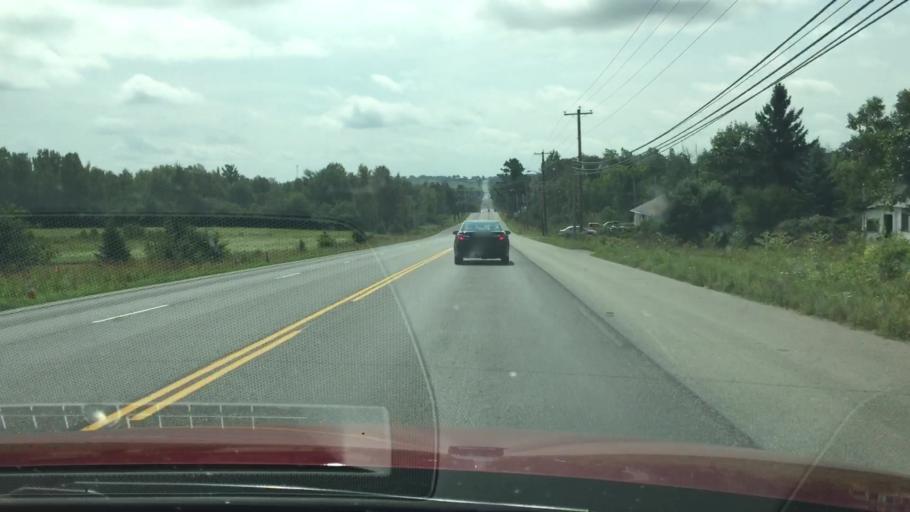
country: US
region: Maine
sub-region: Aroostook County
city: Houlton
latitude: 46.3212
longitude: -67.8415
